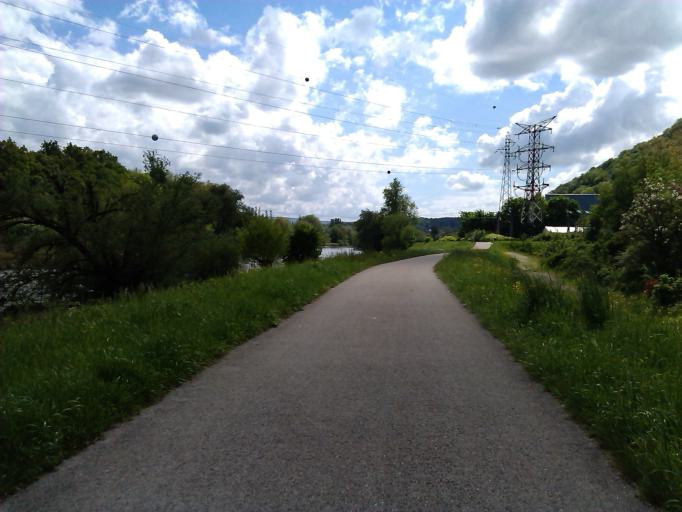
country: FR
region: Franche-Comte
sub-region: Departement du Doubs
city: Bart
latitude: 47.4873
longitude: 6.7718
